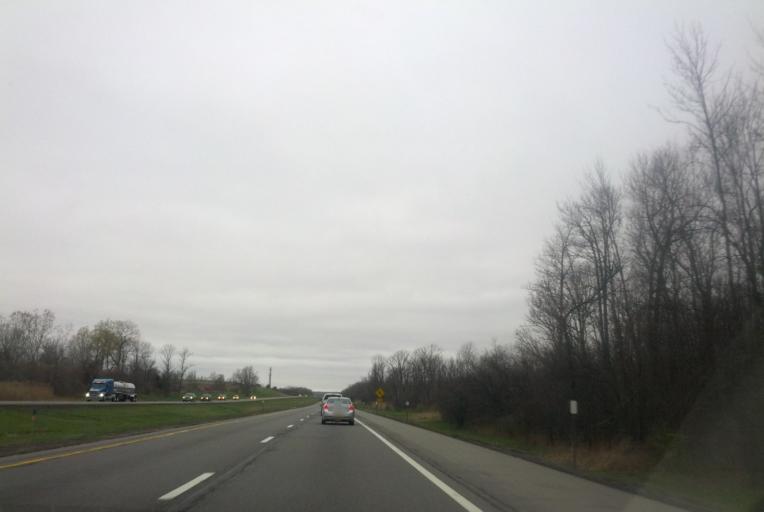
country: US
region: New York
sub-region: Ontario County
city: Manchester
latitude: 42.9876
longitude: -77.3084
